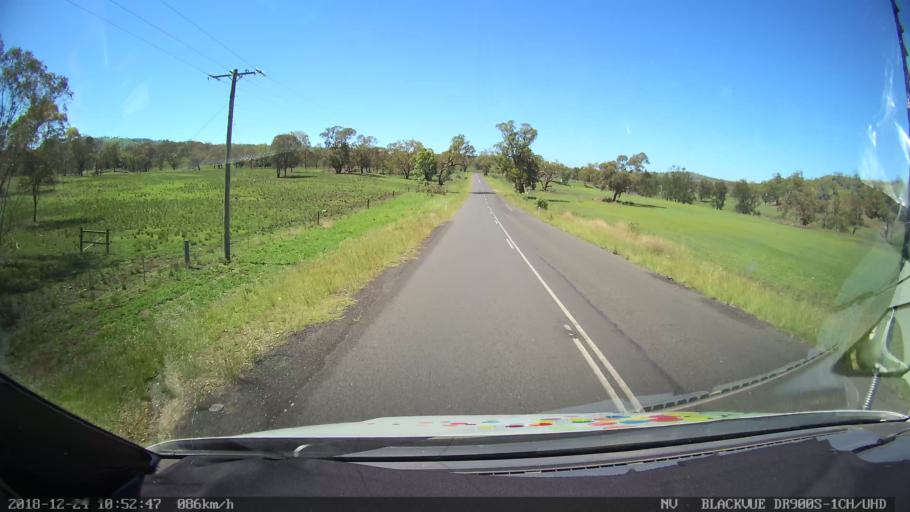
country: AU
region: New South Wales
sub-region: Upper Hunter Shire
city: Merriwa
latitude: -31.9843
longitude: 150.4225
